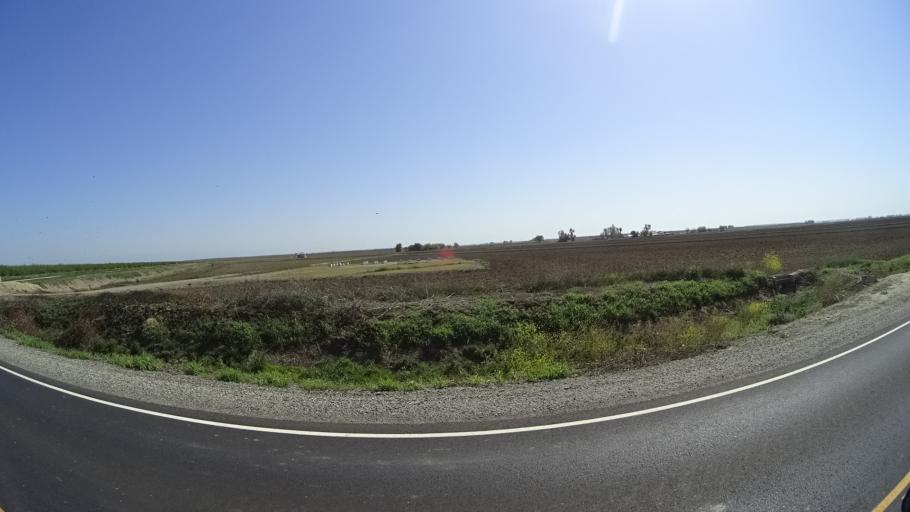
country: US
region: California
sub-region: Glenn County
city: Hamilton City
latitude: 39.6260
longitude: -122.0650
